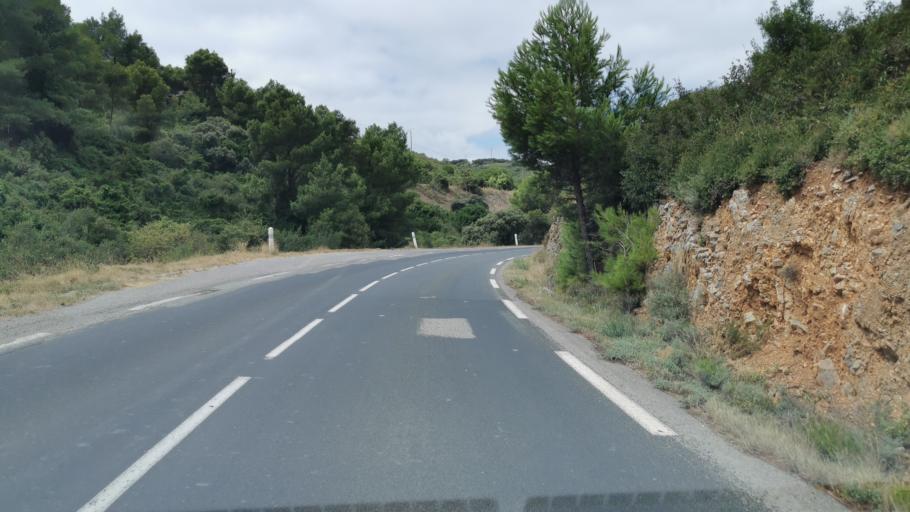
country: FR
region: Languedoc-Roussillon
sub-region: Departement de l'Aude
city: Bizanet
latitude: 43.1681
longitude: 2.9049
